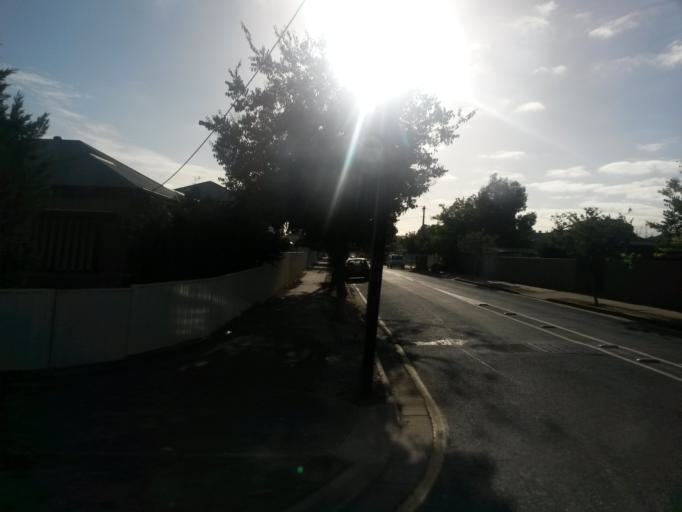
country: AU
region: South Australia
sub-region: Prospect
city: Prospect
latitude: -34.8896
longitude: 138.5763
